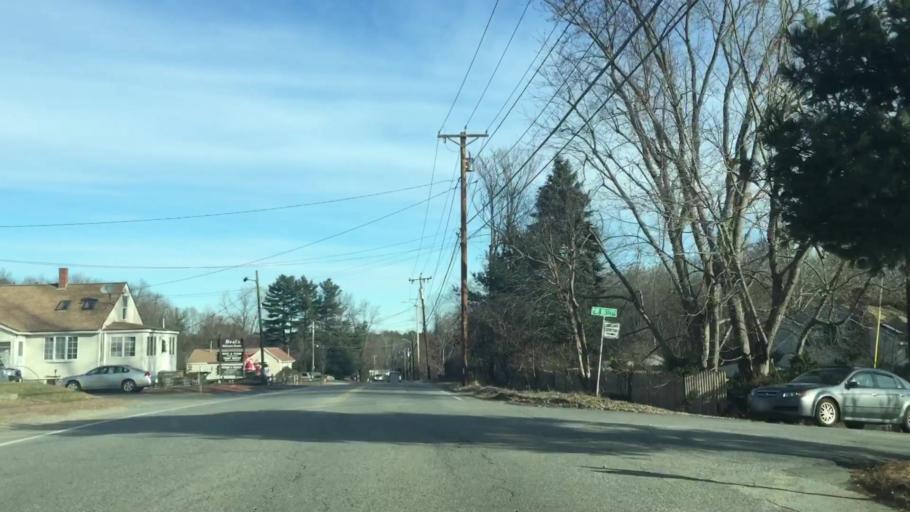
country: US
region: New Hampshire
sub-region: Hillsborough County
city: Pelham
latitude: 42.6905
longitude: -71.3526
